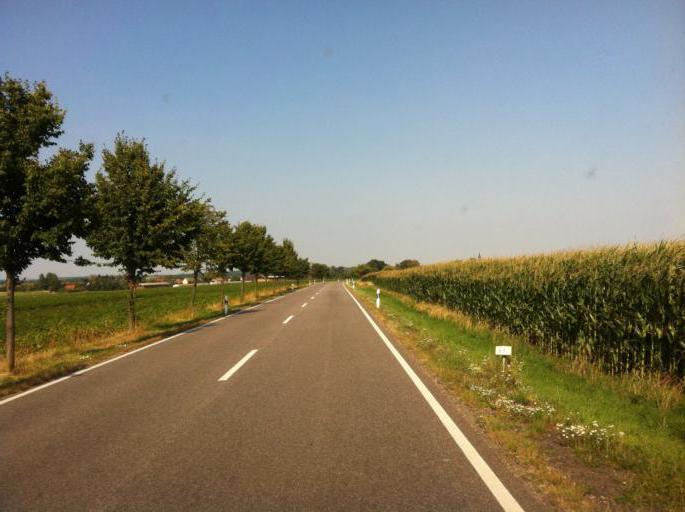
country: DE
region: Thuringia
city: Windischleuba
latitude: 51.0333
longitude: 12.5085
